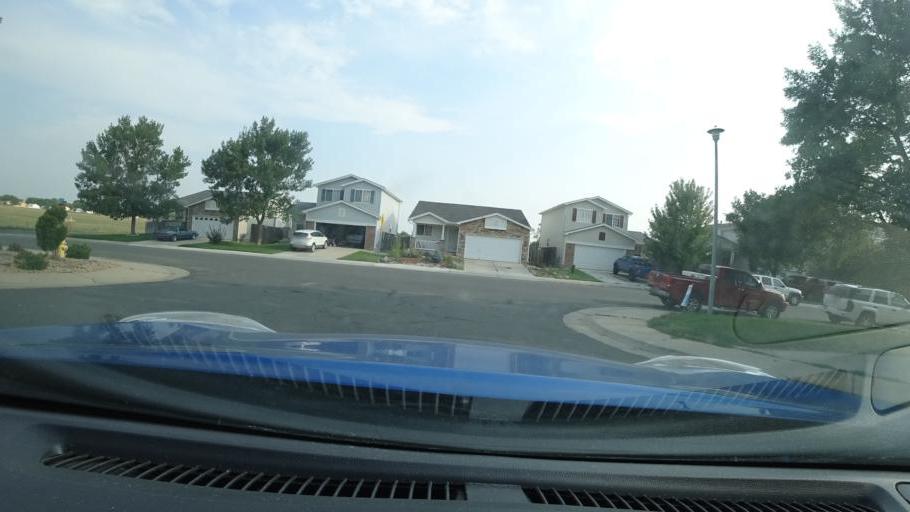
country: US
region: Colorado
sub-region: Adams County
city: Aurora
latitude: 39.7470
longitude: -104.7557
